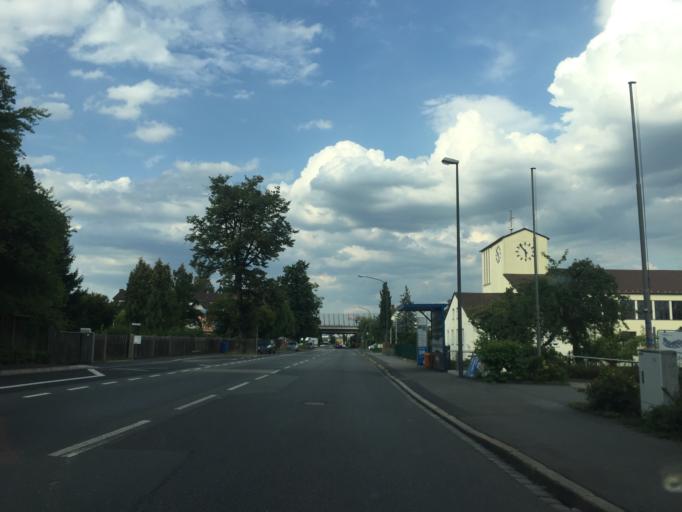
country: DE
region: Bavaria
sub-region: Upper Palatinate
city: Schirmitz
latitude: 49.6555
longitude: 12.1432
